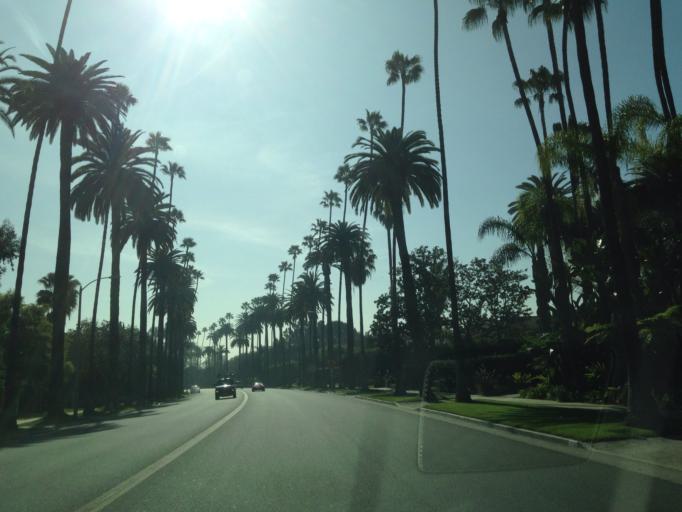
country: US
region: California
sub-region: Los Angeles County
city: Beverly Hills
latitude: 34.0787
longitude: -118.4113
